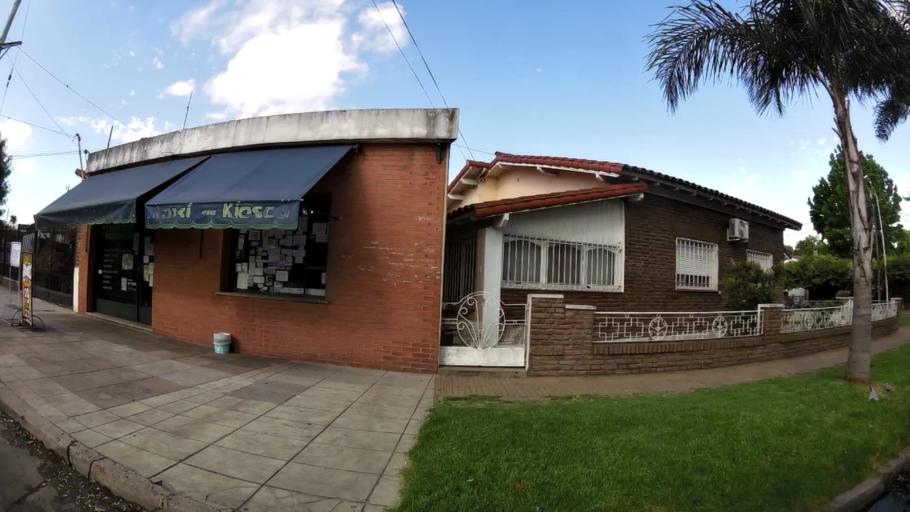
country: AR
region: Buenos Aires
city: San Justo
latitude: -34.6695
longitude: -58.5876
